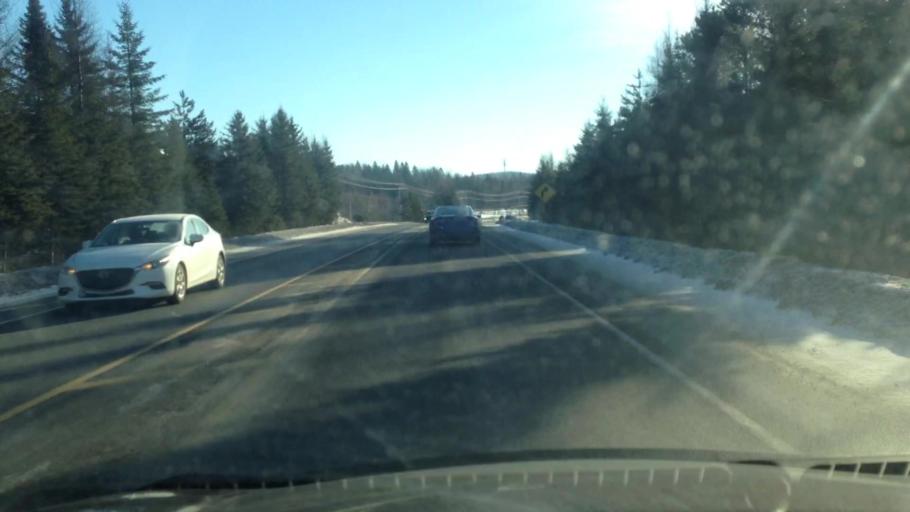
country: CA
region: Quebec
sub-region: Laurentides
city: Saint-Sauveur
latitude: 45.8946
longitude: -74.1999
